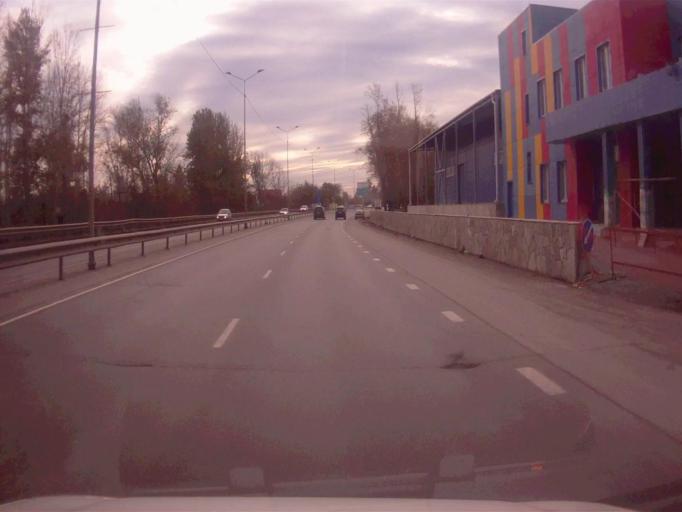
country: RU
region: Chelyabinsk
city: Novosineglazovskiy
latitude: 55.0878
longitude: 61.3986
